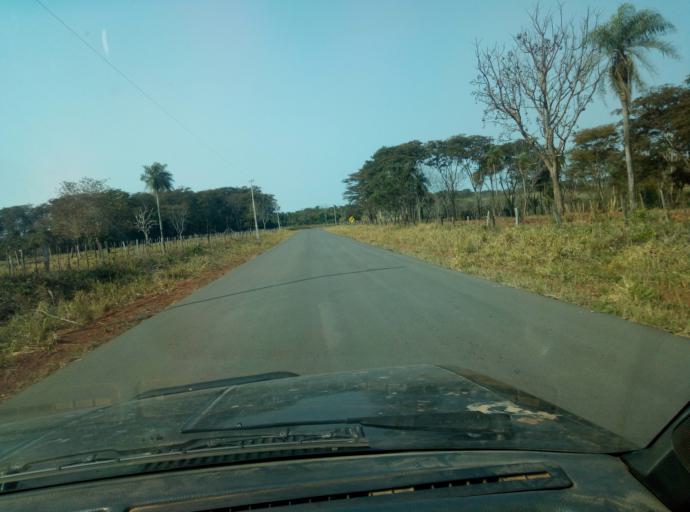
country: PY
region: Caaguazu
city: Carayao
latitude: -25.1954
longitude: -56.3093
